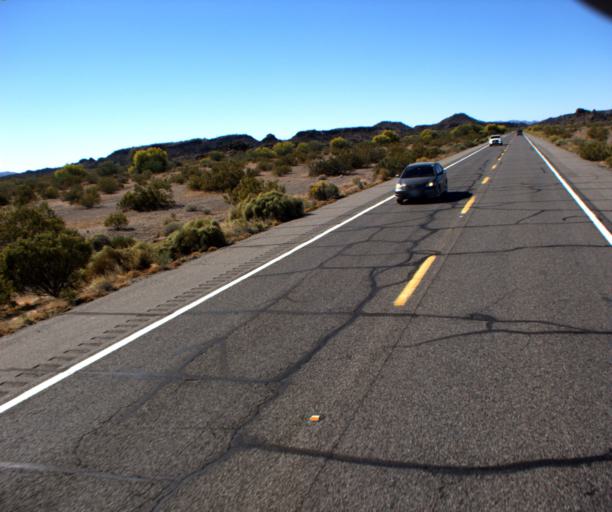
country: US
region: Arizona
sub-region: Pima County
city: Ajo
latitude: 32.5757
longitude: -112.8747
